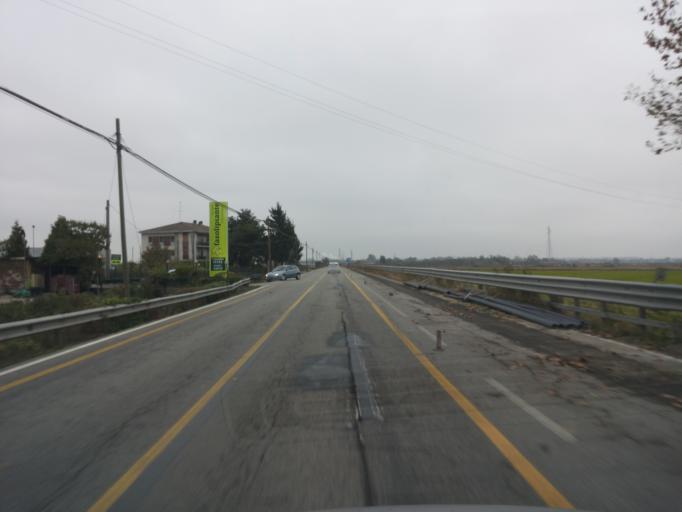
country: IT
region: Piedmont
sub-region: Provincia di Novara
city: Lumellogno
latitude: 45.4143
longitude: 8.5647
